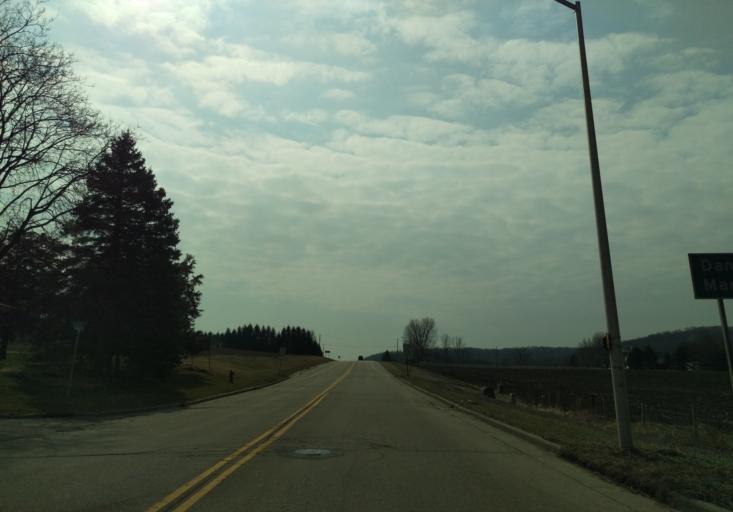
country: US
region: Wisconsin
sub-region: Columbia County
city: Lodi
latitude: 43.3069
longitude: -89.5259
